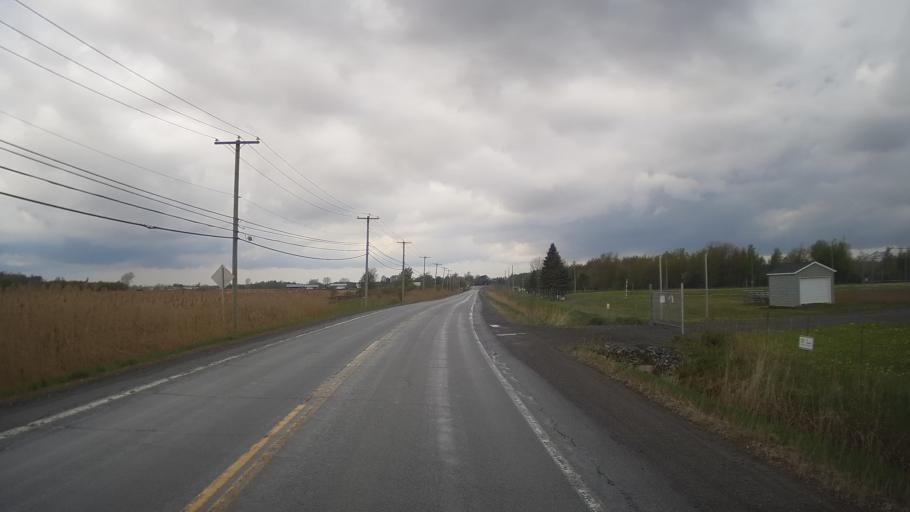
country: CA
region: Quebec
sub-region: Monteregie
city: Farnham
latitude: 45.2875
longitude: -73.0004
